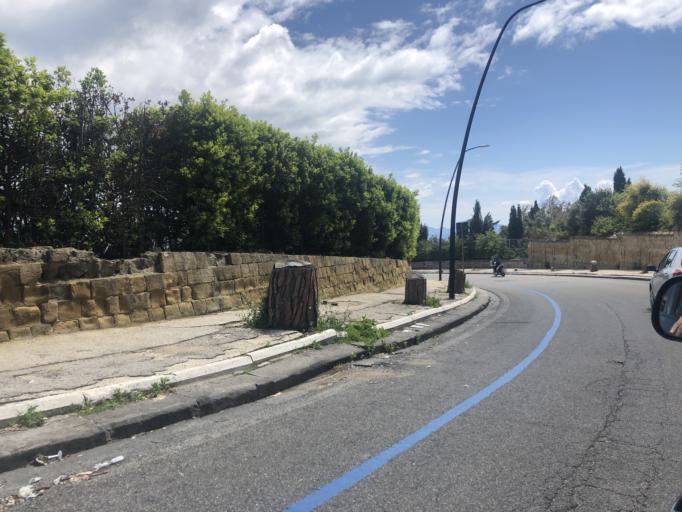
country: IT
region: Campania
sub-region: Provincia di Napoli
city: Bagnoli
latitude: 40.7987
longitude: 14.1815
